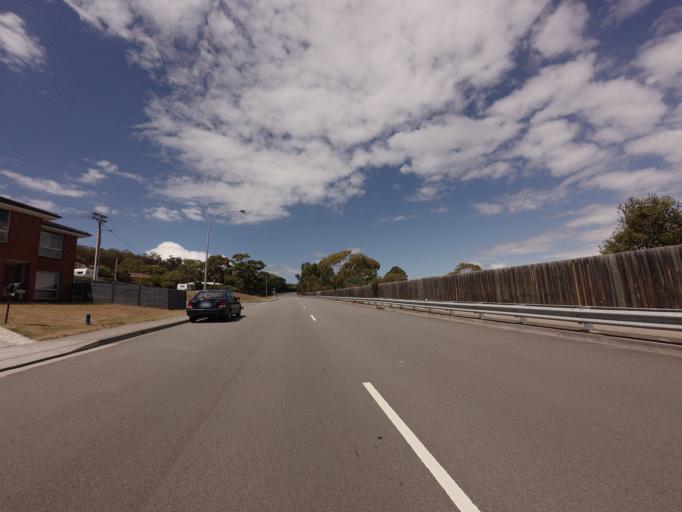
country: AU
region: Tasmania
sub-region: Clarence
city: Howrah
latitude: -42.8944
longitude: 147.4145
